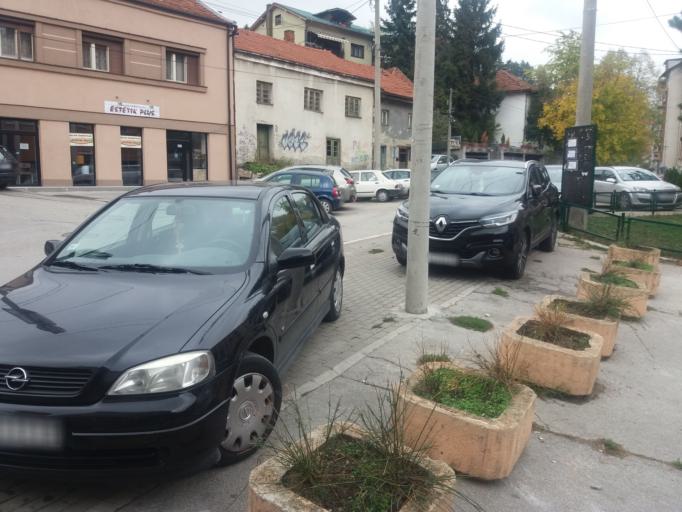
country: RS
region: Central Serbia
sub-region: Zlatiborski Okrug
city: Uzice
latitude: 43.8590
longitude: 19.8482
